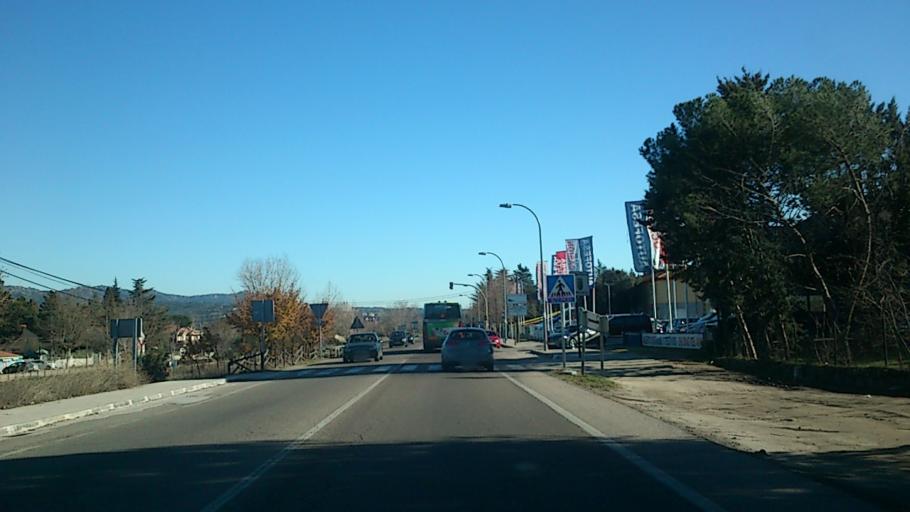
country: ES
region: Madrid
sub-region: Provincia de Madrid
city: Alpedrete
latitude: 40.6406
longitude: -4.0308
